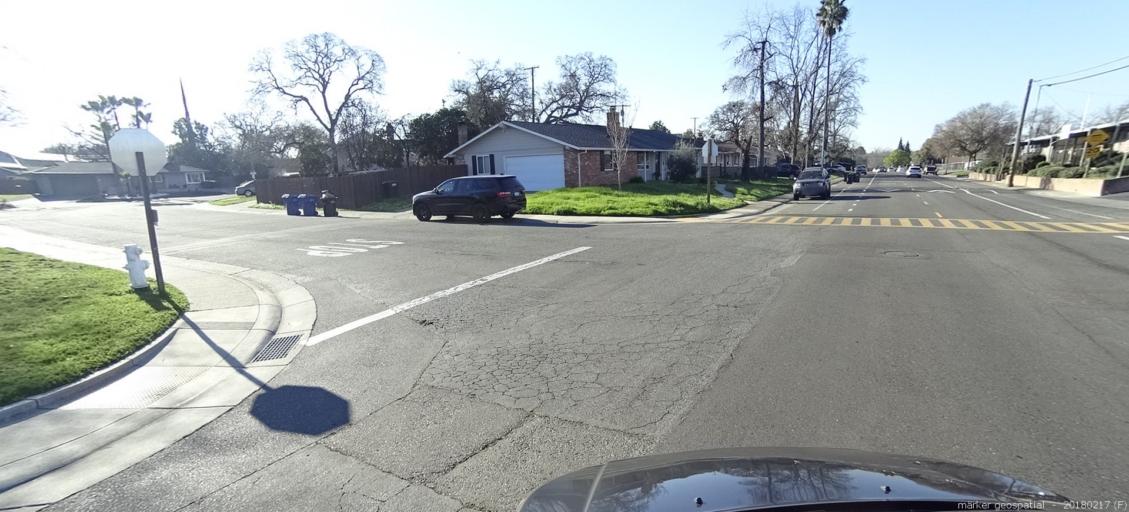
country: US
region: California
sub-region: Sacramento County
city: Folsom
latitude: 38.6750
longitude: -121.1943
